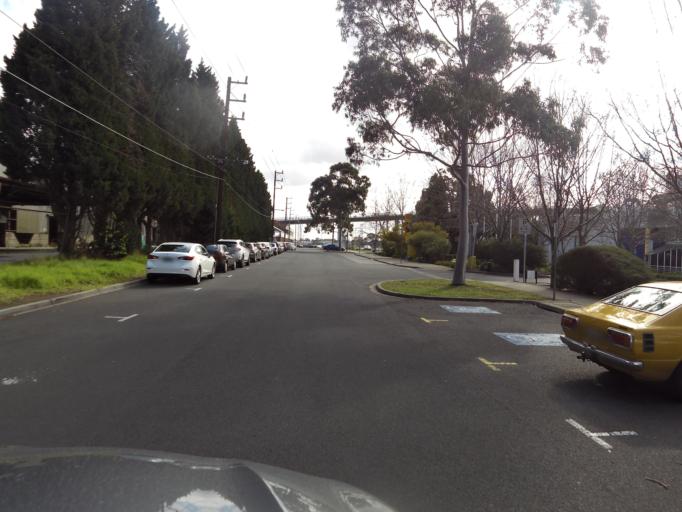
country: AU
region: Victoria
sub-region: Hobsons Bay
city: Spotswood
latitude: -37.8320
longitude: 144.8926
